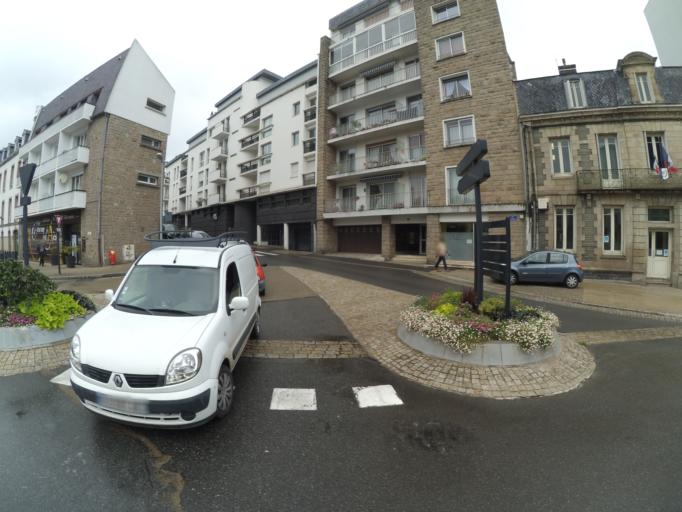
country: FR
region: Brittany
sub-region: Departement du Finistere
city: Morlaix
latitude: 48.5816
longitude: -3.8318
